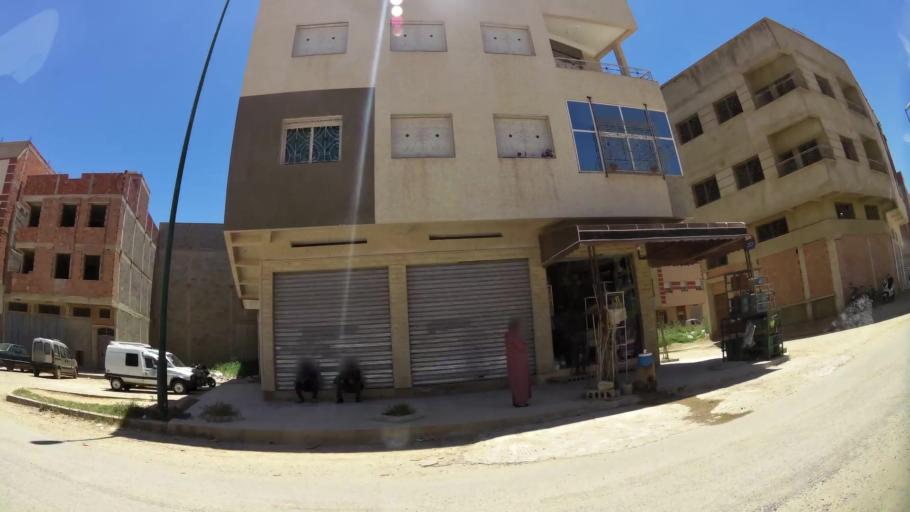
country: MA
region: Meknes-Tafilalet
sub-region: Meknes
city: Meknes
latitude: 33.8681
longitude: -5.5680
